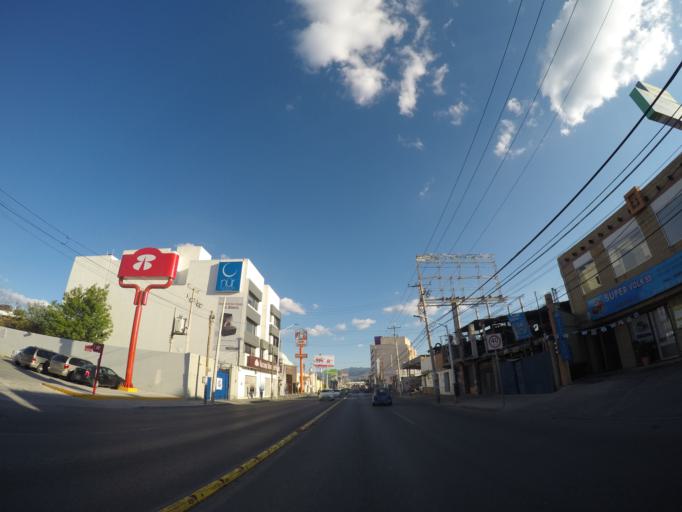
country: MX
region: San Luis Potosi
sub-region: San Luis Potosi
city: San Luis Potosi
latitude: 22.1634
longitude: -101.0008
